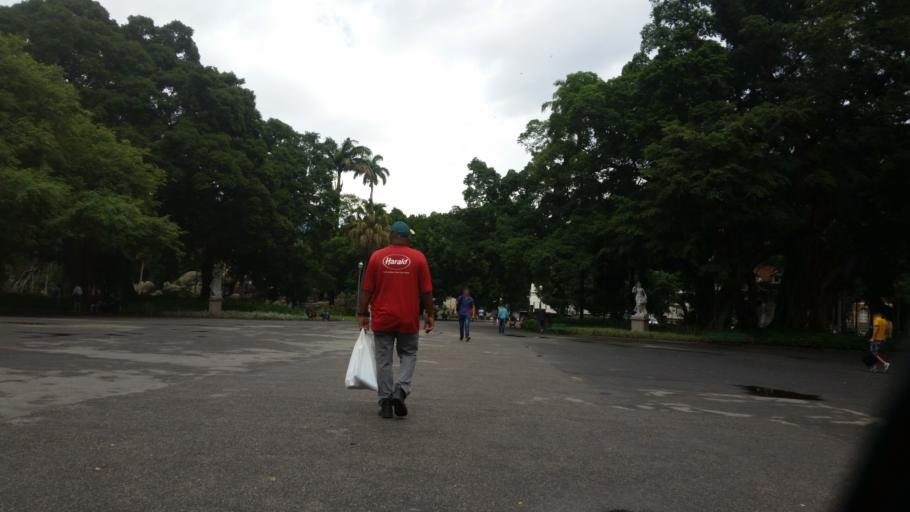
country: BR
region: Rio de Janeiro
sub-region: Rio De Janeiro
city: Rio de Janeiro
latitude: -22.9066
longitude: -43.1887
